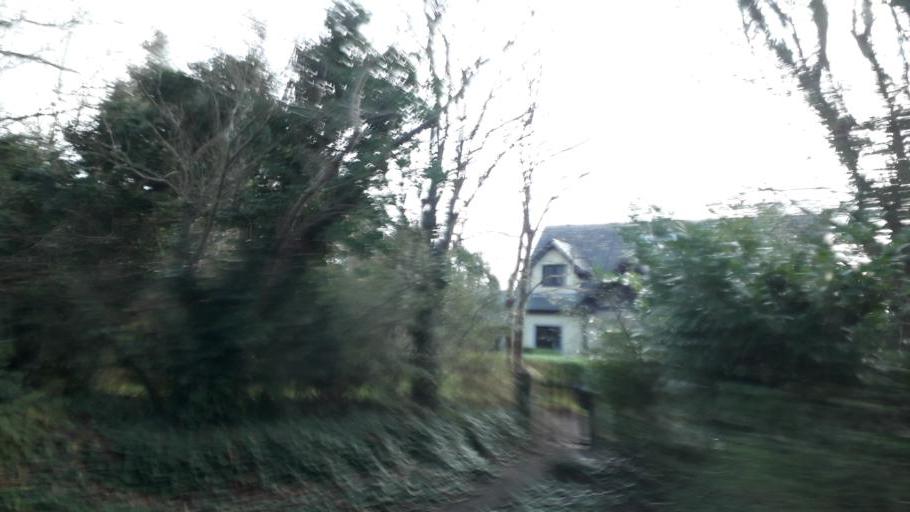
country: IE
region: Leinster
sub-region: Fingal County
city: Skerries
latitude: 53.5699
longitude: -6.1307
